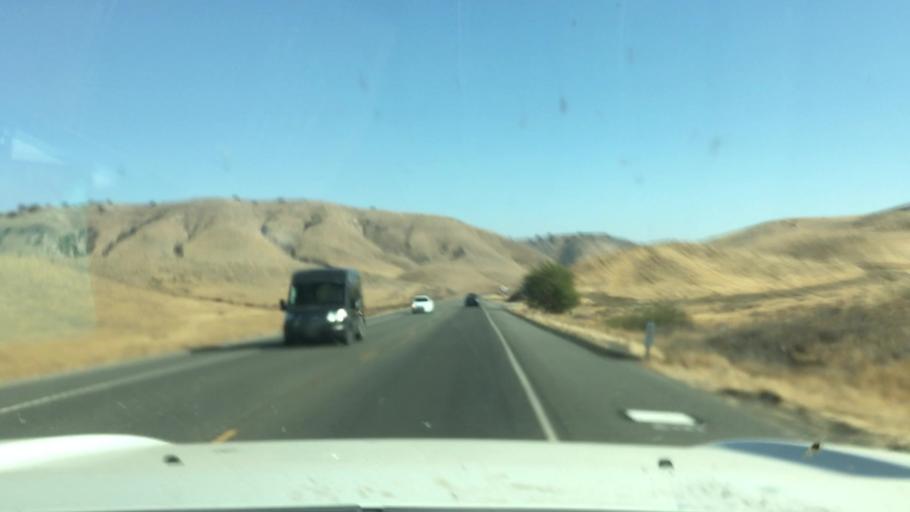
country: US
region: California
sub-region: San Luis Obispo County
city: Shandon
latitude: 35.7433
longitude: -120.2324
